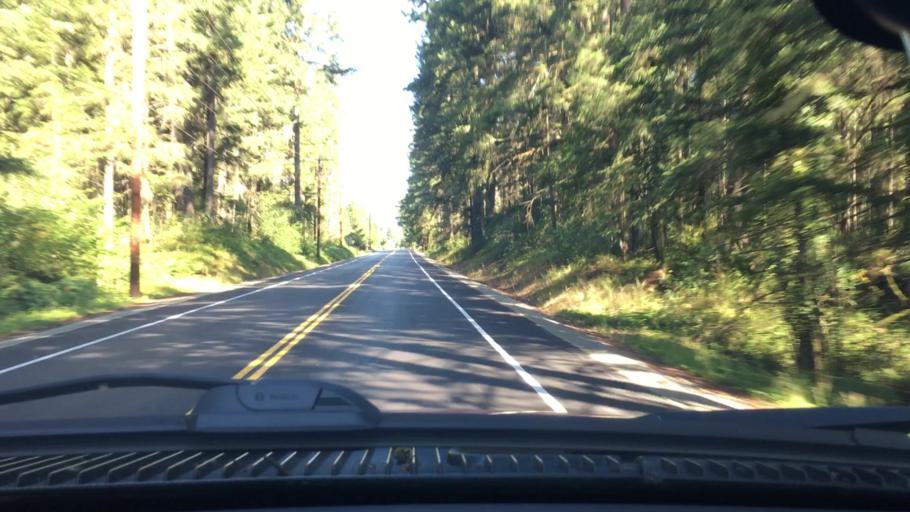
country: US
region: Washington
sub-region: King County
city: Lake Morton-Berrydale
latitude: 47.3200
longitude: -122.1052
